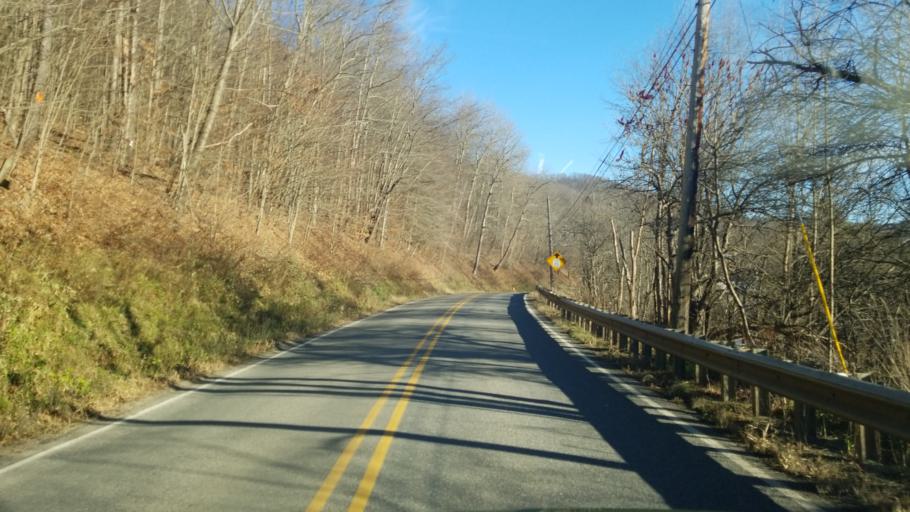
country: US
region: Pennsylvania
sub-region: Potter County
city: Coudersport
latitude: 41.6322
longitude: -78.0967
